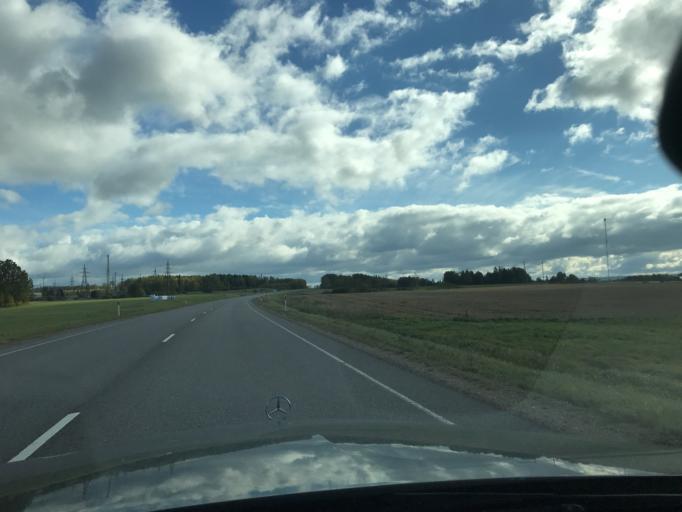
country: EE
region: Vorumaa
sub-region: Voru linn
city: Voru
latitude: 57.8582
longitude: 27.0143
